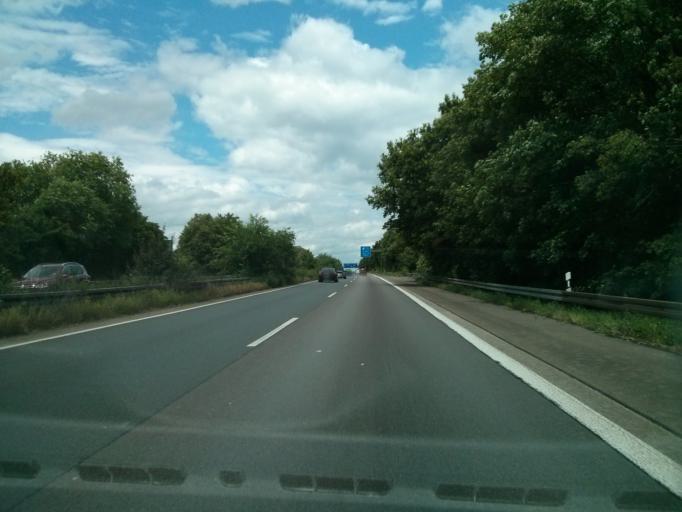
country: DE
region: North Rhine-Westphalia
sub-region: Regierungsbezirk Dusseldorf
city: Krefeld
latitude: 51.3286
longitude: 6.6293
